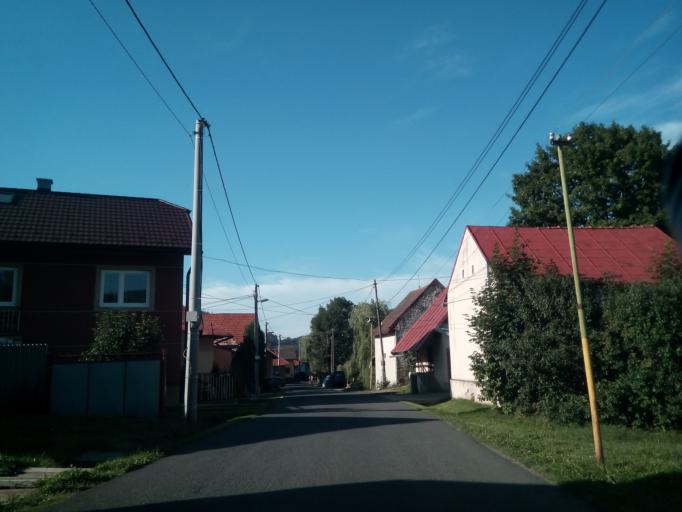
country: SK
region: Presovsky
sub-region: Okres Poprad
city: Svit
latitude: 48.9902
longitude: 20.2409
